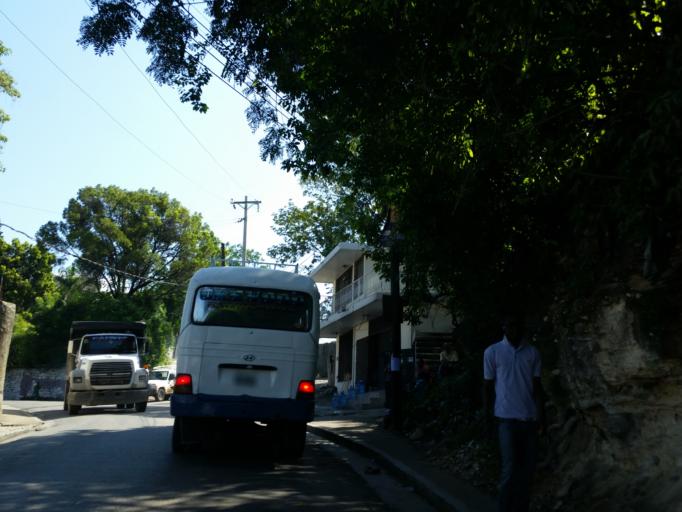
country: HT
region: Ouest
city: Delmas 73
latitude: 18.5299
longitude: -72.2978
